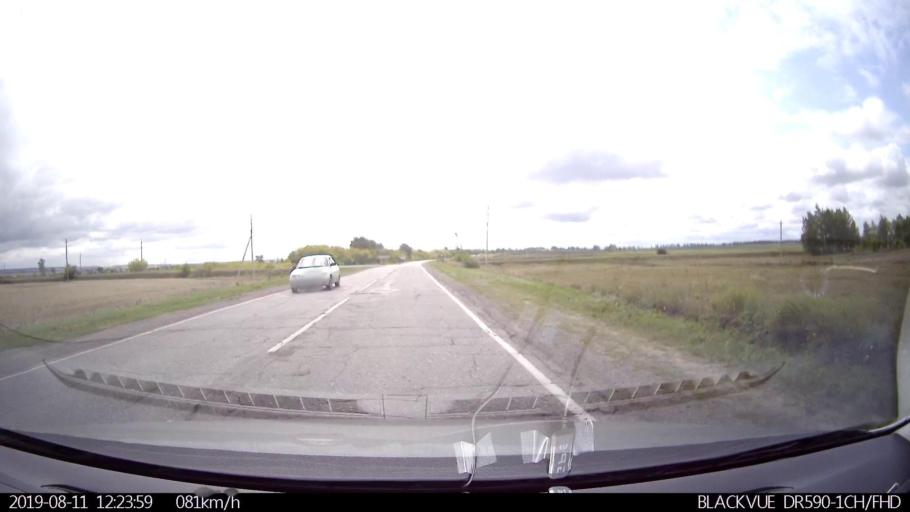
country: RU
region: Ulyanovsk
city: Ignatovka
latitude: 53.8887
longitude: 47.9502
